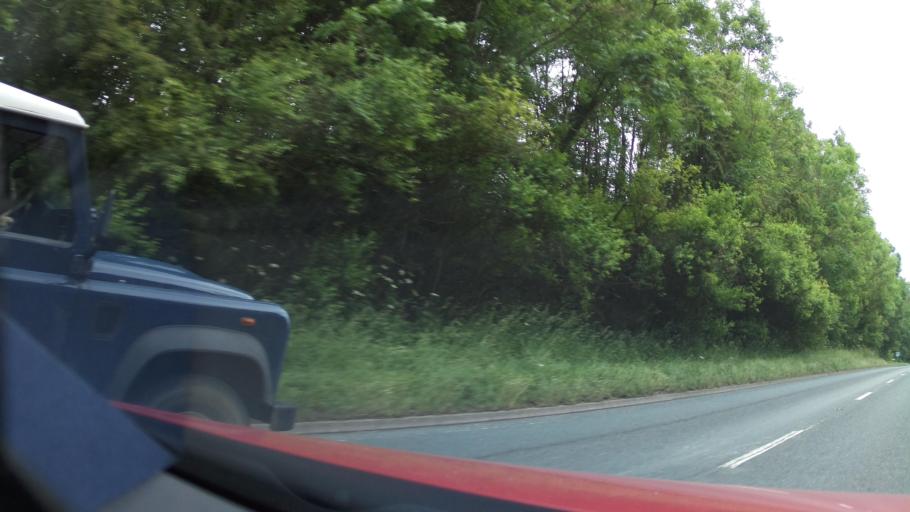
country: GB
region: England
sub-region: Staffordshire
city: Mayfield
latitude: 52.9924
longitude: -1.7482
